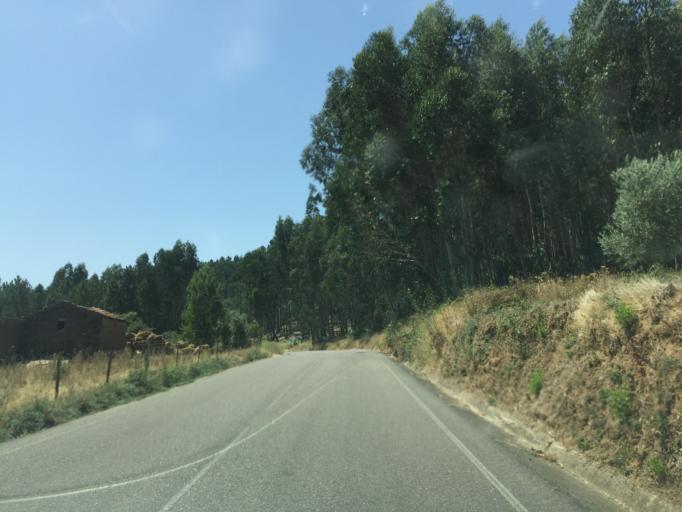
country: PT
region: Santarem
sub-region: Ferreira do Zezere
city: Ferreira do Zezere
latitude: 39.6131
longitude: -8.3117
